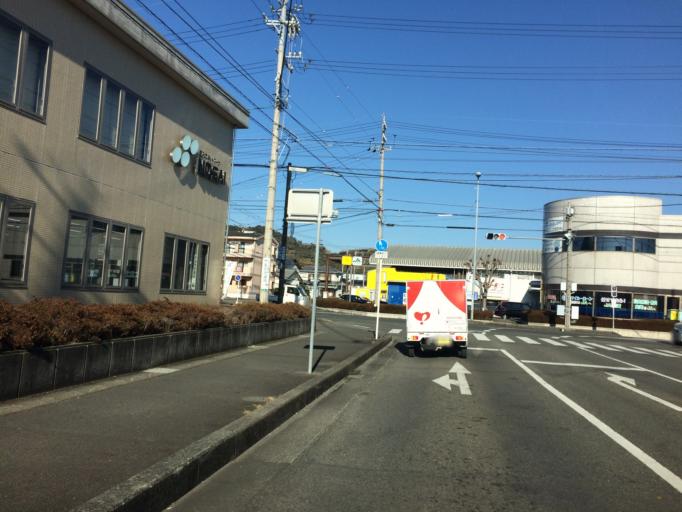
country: JP
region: Shizuoka
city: Shimada
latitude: 34.8383
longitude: 138.2095
